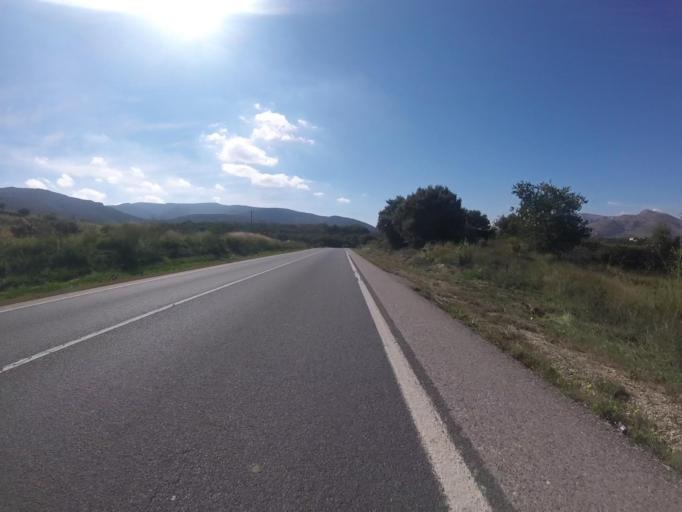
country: ES
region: Valencia
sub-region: Provincia de Castello
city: Albocasser
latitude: 40.3337
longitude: -0.0135
